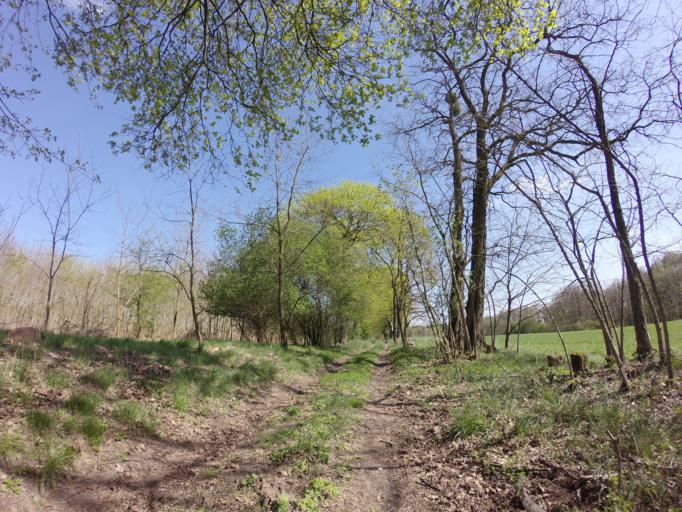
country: PL
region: West Pomeranian Voivodeship
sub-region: Powiat choszczenski
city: Choszczno
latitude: 53.1795
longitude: 15.3355
